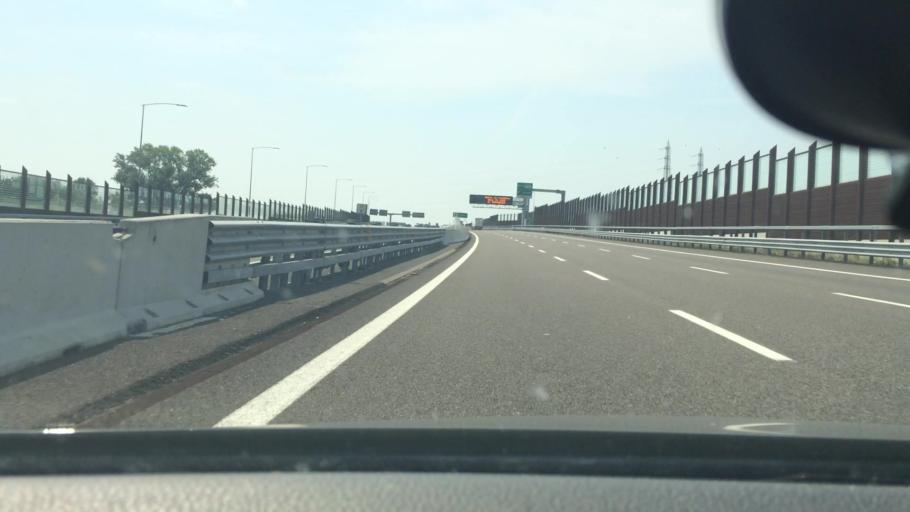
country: IT
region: Lombardy
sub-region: Citta metropolitana di Milano
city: Pozzuolo Martesana
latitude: 45.5107
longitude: 9.4407
